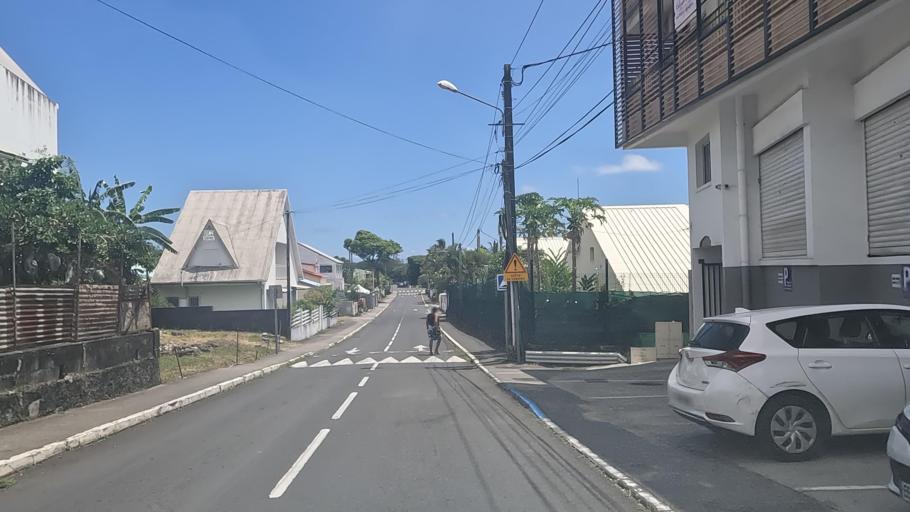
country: RE
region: Reunion
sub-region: Reunion
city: Saint-Benoit
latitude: -21.0322
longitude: 55.7120
